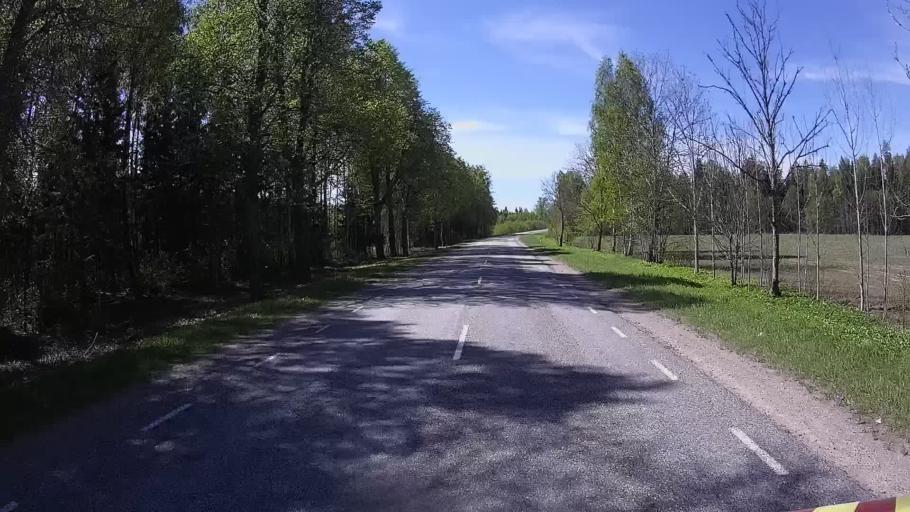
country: EE
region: Polvamaa
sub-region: Raepina vald
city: Rapina
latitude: 57.9840
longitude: 27.3146
